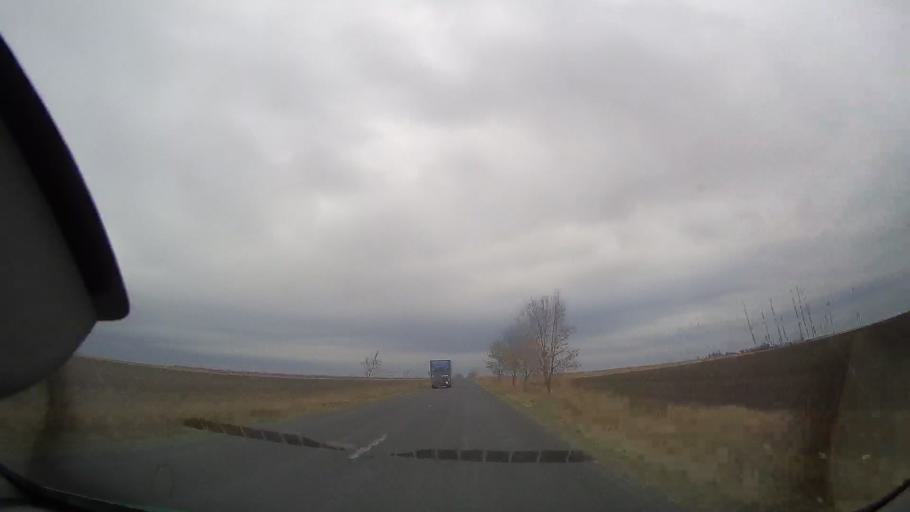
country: RO
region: Buzau
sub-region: Comuna Padina
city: Padina
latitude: 44.7946
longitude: 27.1404
